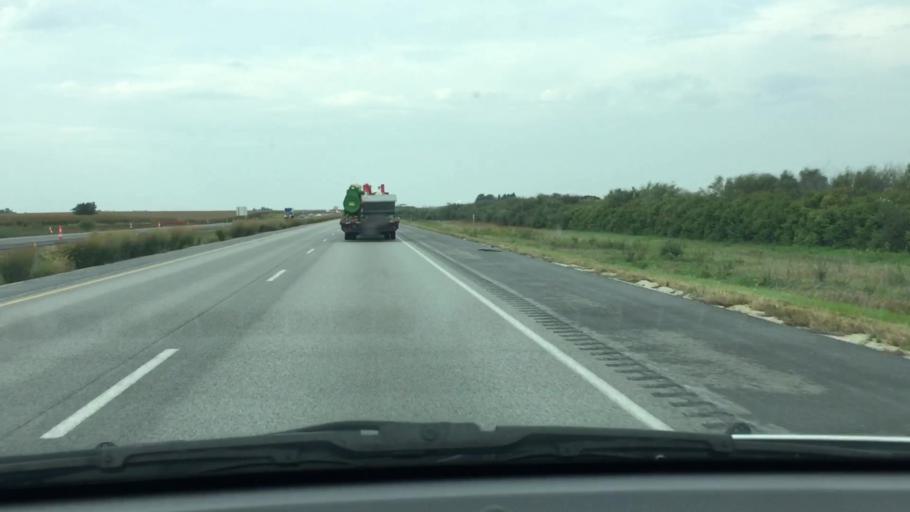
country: US
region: Iowa
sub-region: Scott County
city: Walcott
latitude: 41.6033
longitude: -90.7092
